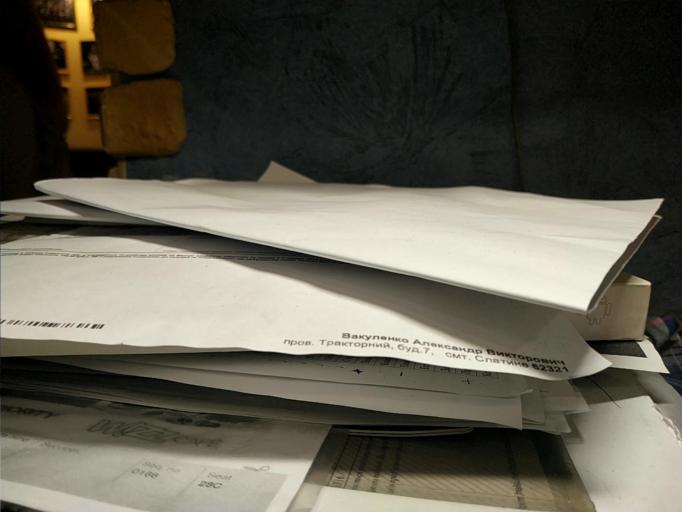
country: RU
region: Tverskaya
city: Zubtsov
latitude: 56.0923
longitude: 34.7329
